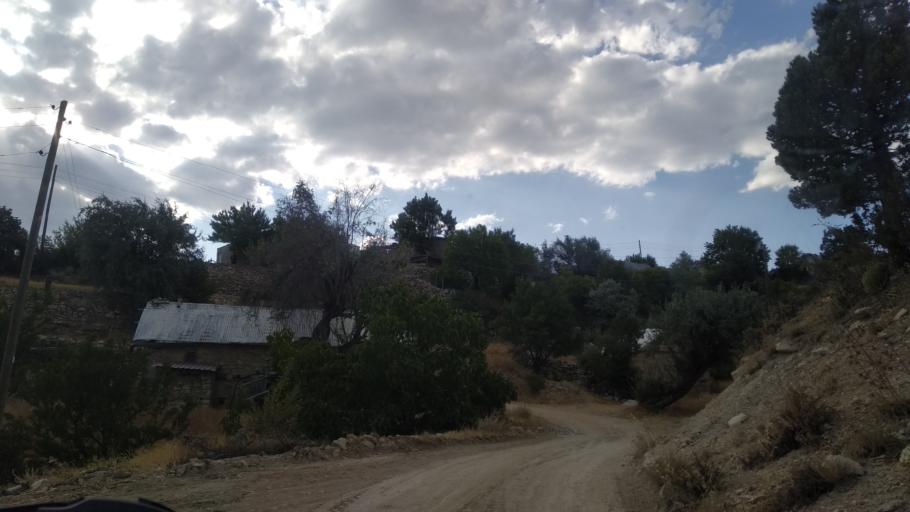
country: TR
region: Mersin
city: Sarikavak
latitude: 36.6010
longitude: 33.7255
